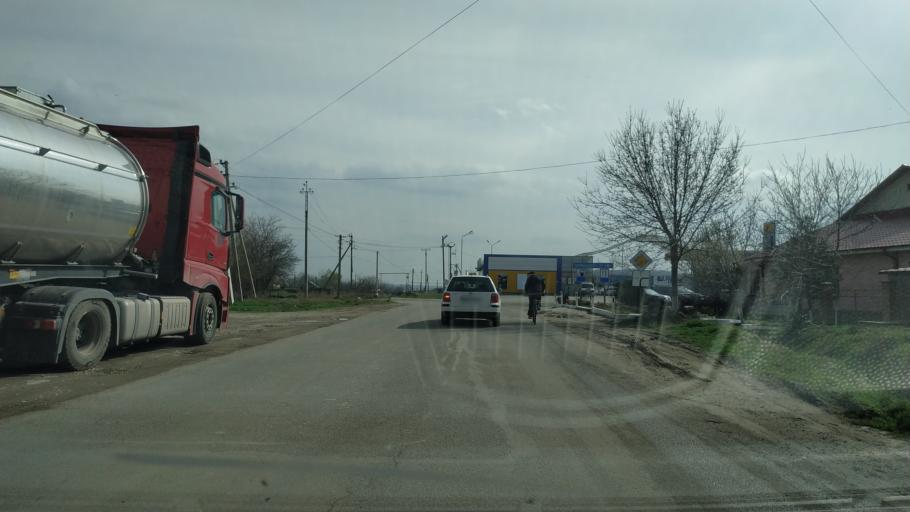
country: MD
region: Gagauzia
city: Vulcanesti
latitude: 45.6777
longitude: 28.4110
